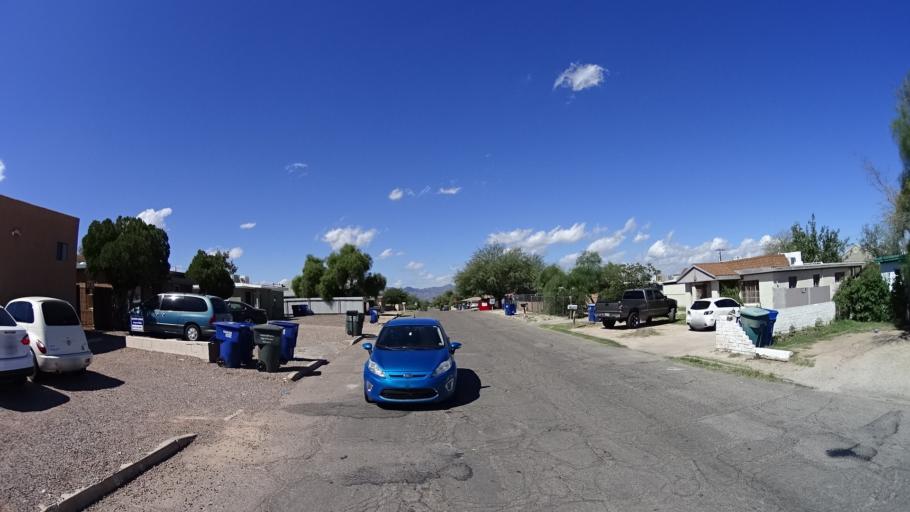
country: US
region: Arizona
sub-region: Pima County
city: Tucson
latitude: 32.2426
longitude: -110.9599
